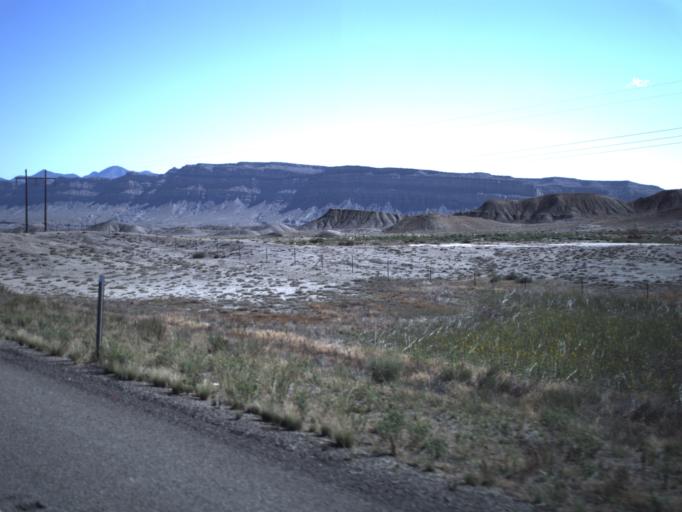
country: US
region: Utah
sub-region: Carbon County
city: East Carbon City
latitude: 39.2175
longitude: -110.3386
